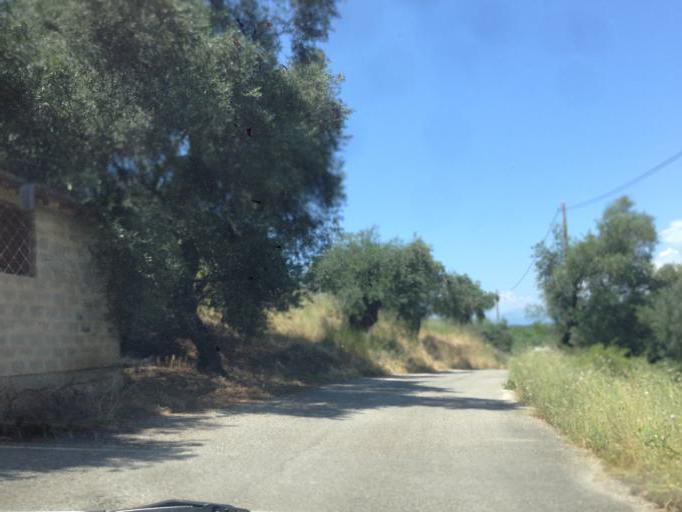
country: GR
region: Ionian Islands
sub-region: Nomos Kerkyras
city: Acharavi
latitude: 39.8045
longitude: 19.8504
